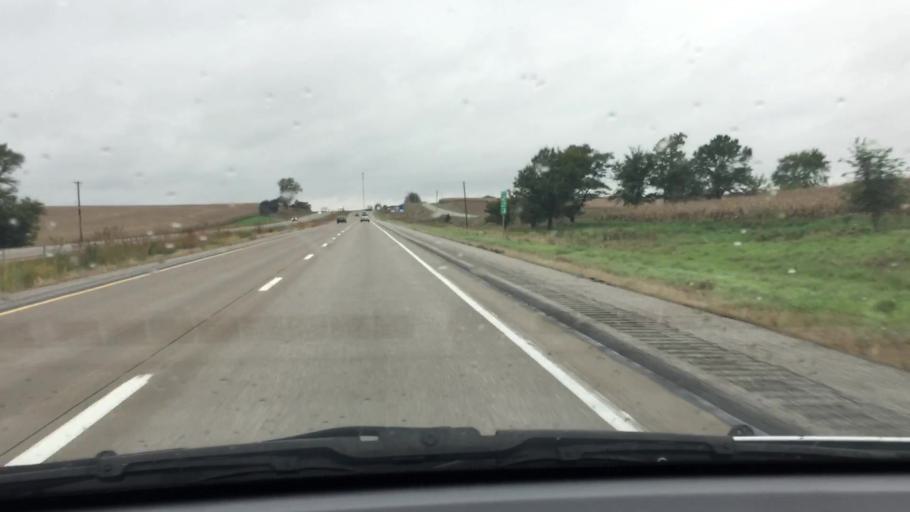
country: US
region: Iowa
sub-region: Iowa County
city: Williamsburg
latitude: 41.6875
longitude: -91.9482
